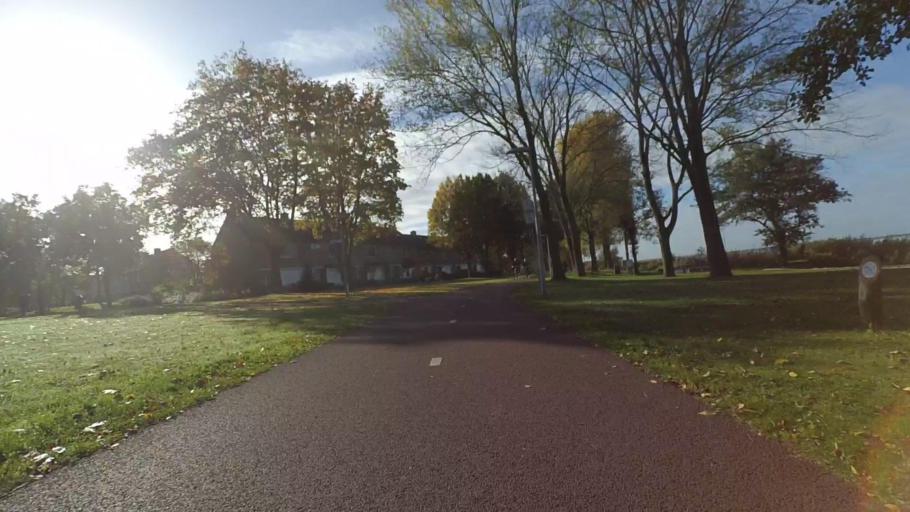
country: NL
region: Gelderland
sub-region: Gemeente Harderwijk
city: Harderwijk
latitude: 52.3426
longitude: 5.6079
